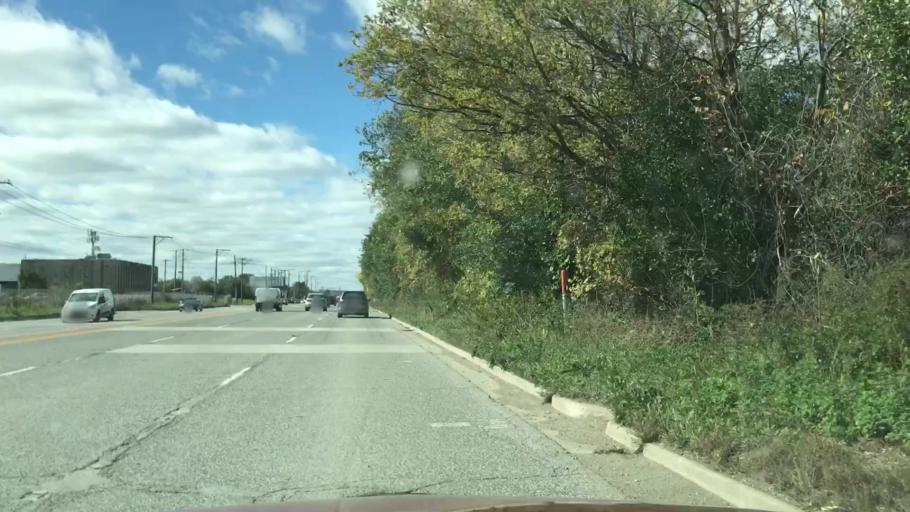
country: US
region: Illinois
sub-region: Cook County
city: Elk Grove Village
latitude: 42.0084
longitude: -87.9282
